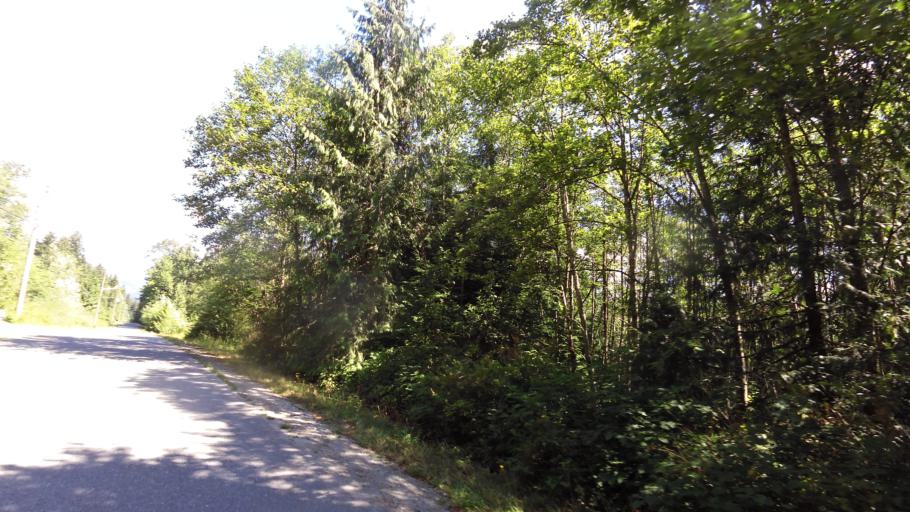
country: CA
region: British Columbia
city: Aldergrove
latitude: 49.2342
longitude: -122.3691
